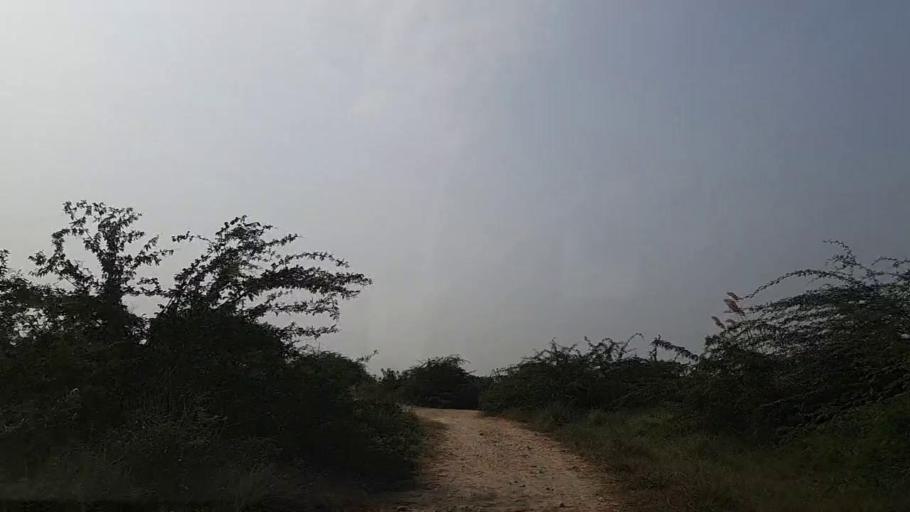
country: PK
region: Sindh
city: Thatta
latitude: 24.6638
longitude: 67.7765
